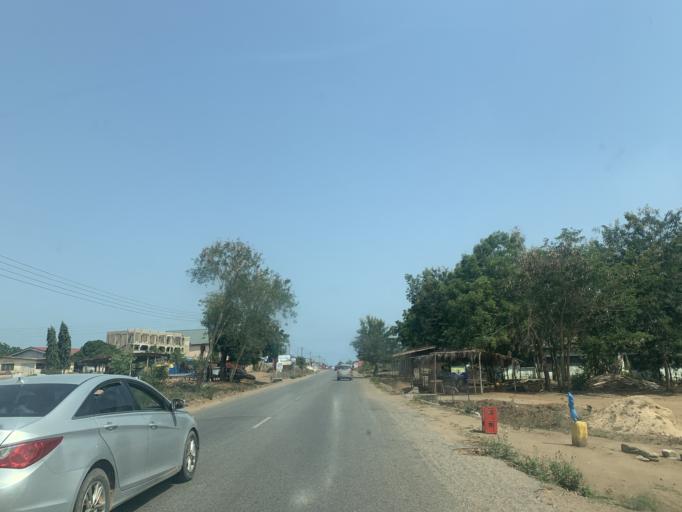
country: GH
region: Central
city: Winneba
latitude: 5.3996
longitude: -0.6504
